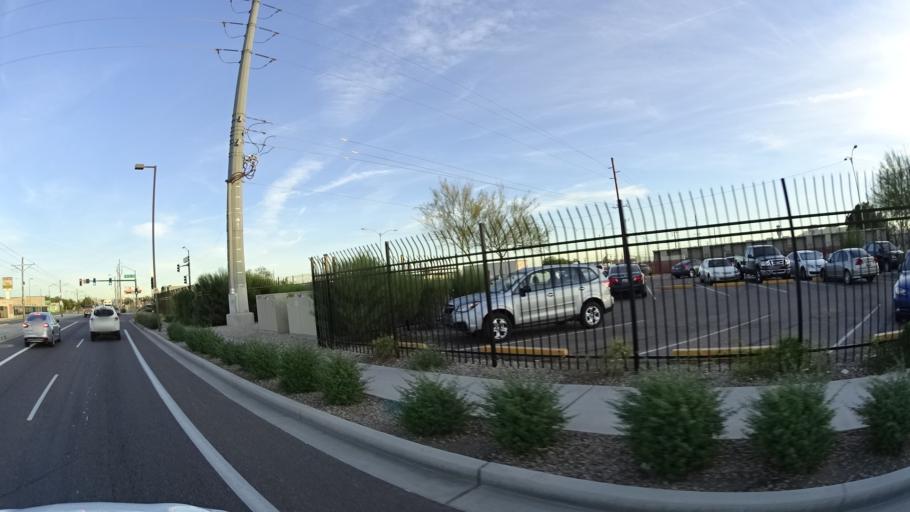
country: US
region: Arizona
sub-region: Maricopa County
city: Phoenix
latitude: 33.4481
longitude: -112.0044
